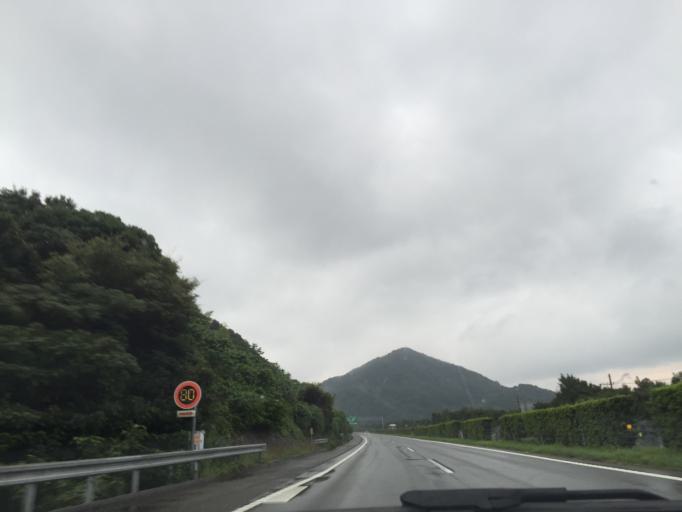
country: JP
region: Tokushima
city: Narutocho-mitsuishi
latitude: 34.2178
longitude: 134.6249
